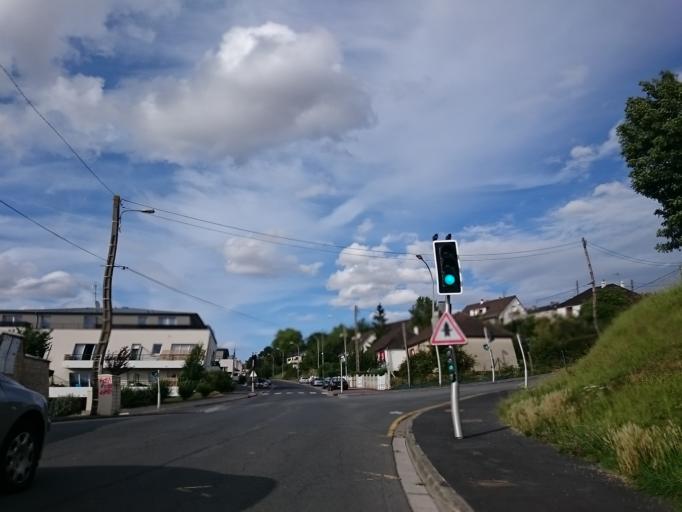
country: FR
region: Lower Normandy
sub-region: Departement du Calvados
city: Fleury-sur-Orne
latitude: 49.1457
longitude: -0.3798
